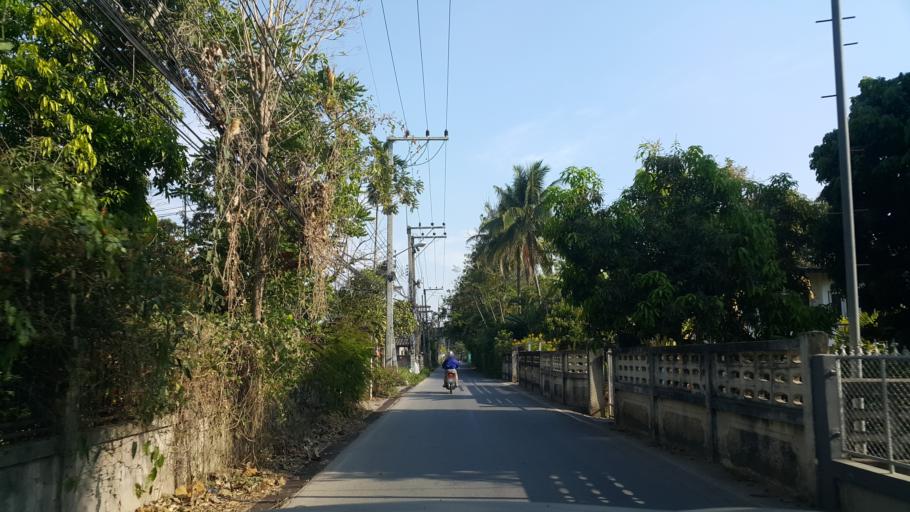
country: TH
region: Chiang Mai
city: San Sai
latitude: 18.8561
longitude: 99.0410
